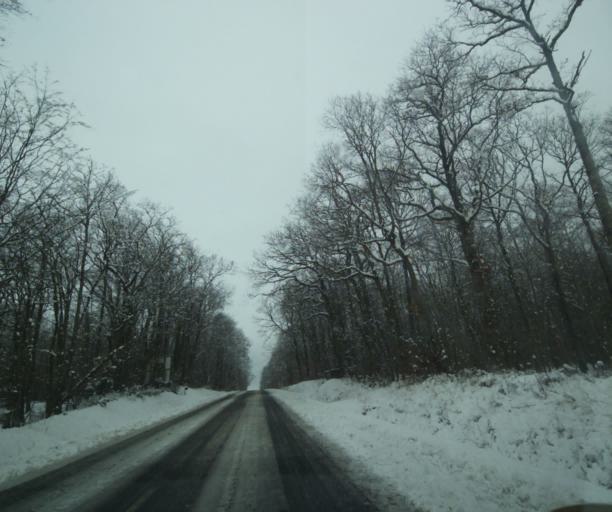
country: FR
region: Champagne-Ardenne
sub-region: Departement de la Haute-Marne
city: Montier-en-Der
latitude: 48.5264
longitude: 4.7486
